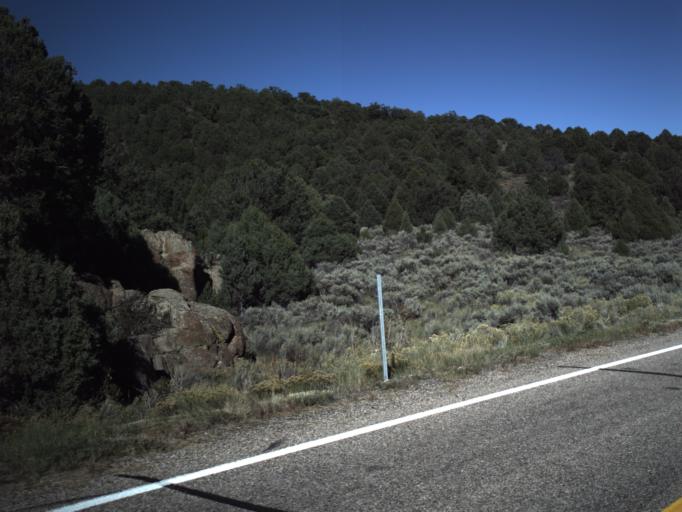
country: US
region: Utah
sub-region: Garfield County
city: Panguitch
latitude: 37.7616
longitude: -112.5104
